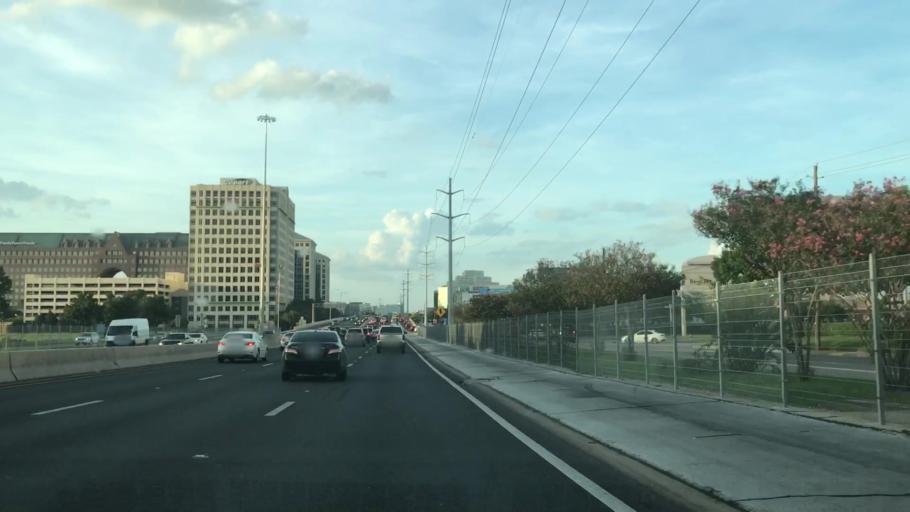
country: US
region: Texas
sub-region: Dallas County
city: Addison
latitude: 32.9354
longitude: -96.8219
